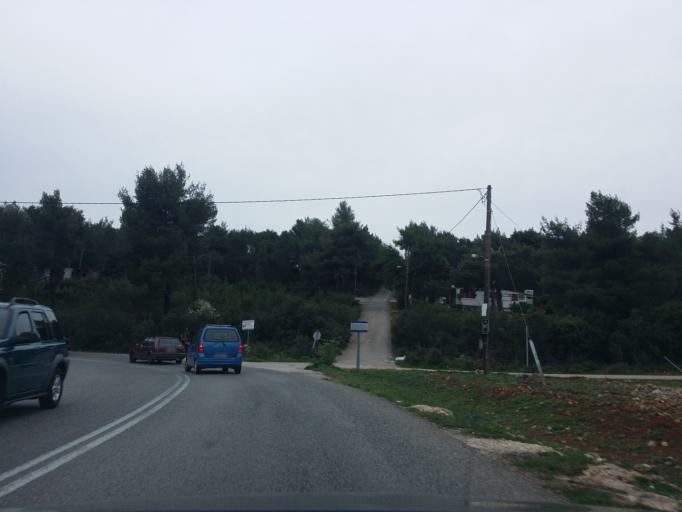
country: GR
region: Attica
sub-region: Nomarchia Dytikis Attikis
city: Vilia
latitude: 38.1277
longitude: 23.4106
